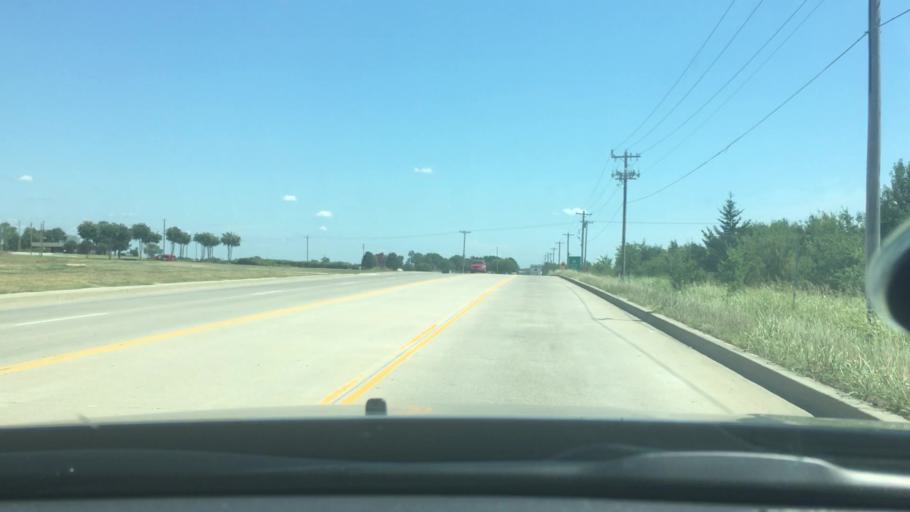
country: US
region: Oklahoma
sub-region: Bryan County
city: Calera
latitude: 33.9510
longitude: -96.4094
